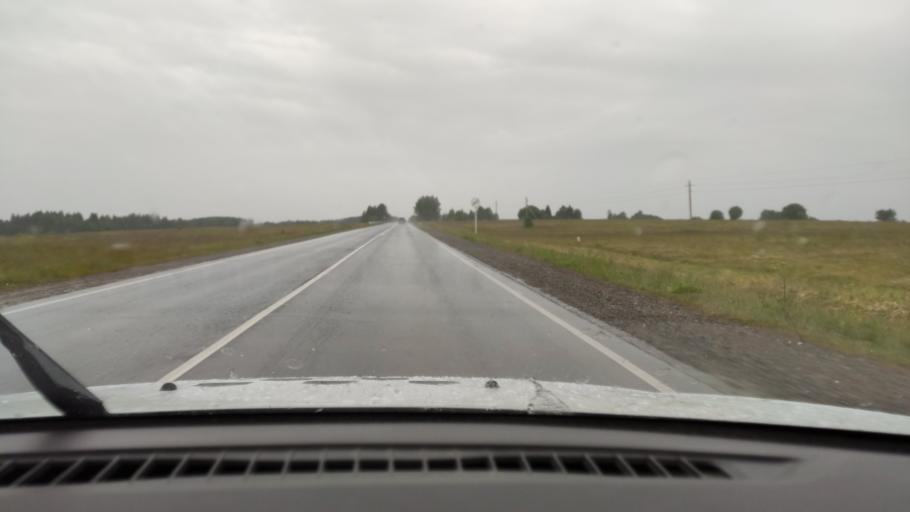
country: RU
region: Perm
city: Ocher
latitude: 57.4587
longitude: 54.4847
